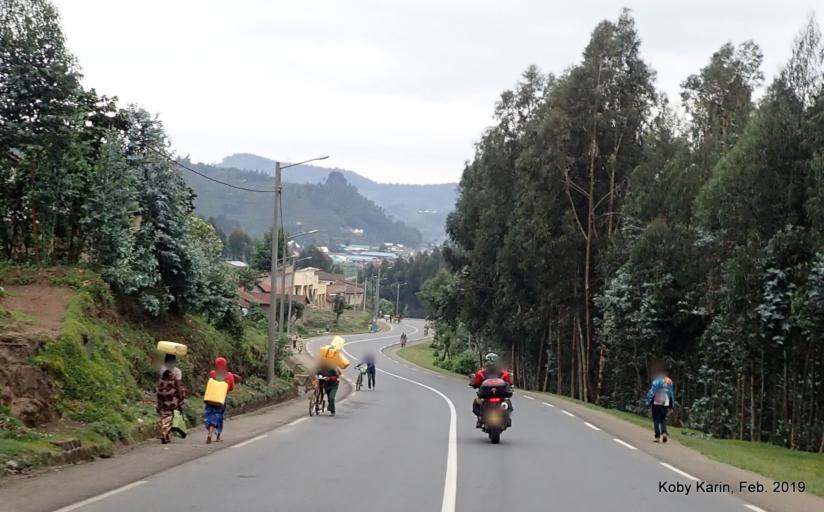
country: RW
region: Northern Province
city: Musanze
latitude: -1.6191
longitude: 29.4578
